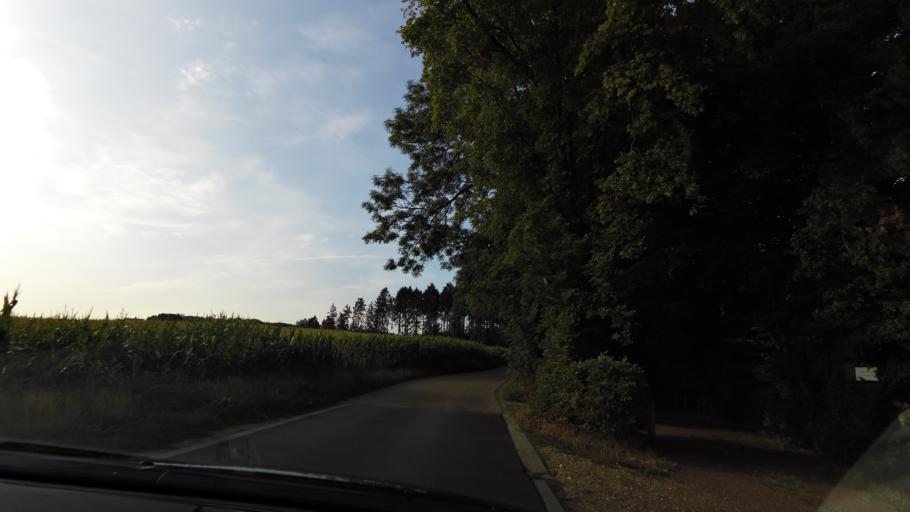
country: BE
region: Wallonia
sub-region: Province de Liege
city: Plombieres
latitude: 50.7807
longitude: 5.9660
